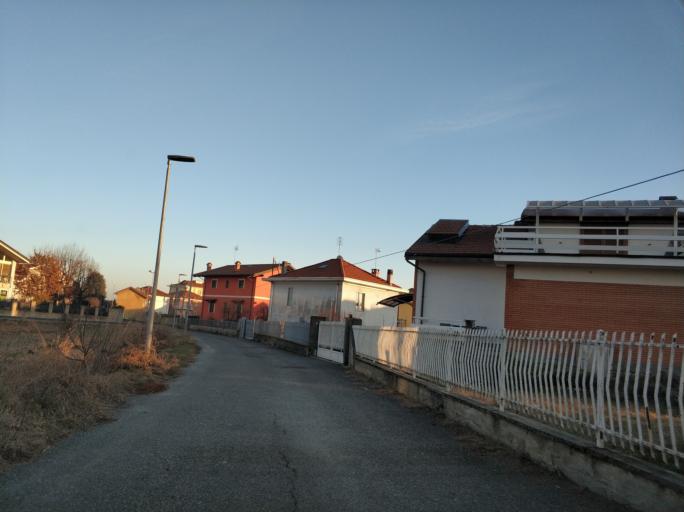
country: IT
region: Piedmont
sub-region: Provincia di Torino
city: Caselle Torinese
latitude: 45.1825
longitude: 7.6383
